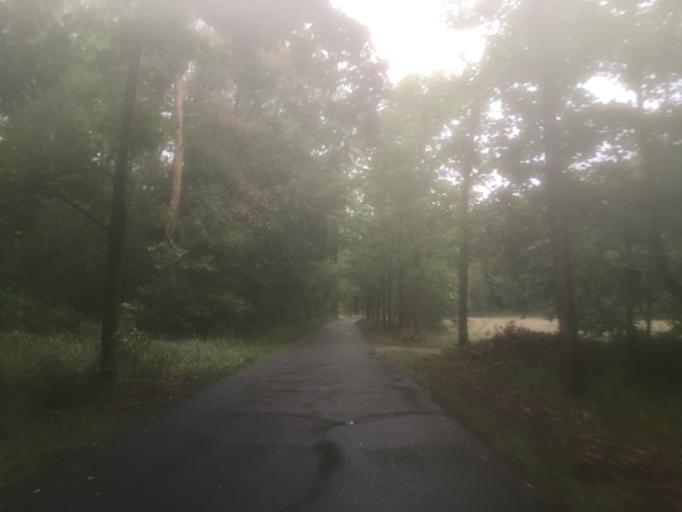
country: DE
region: Brandenburg
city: Zehdenick
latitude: 53.0147
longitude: 13.3128
